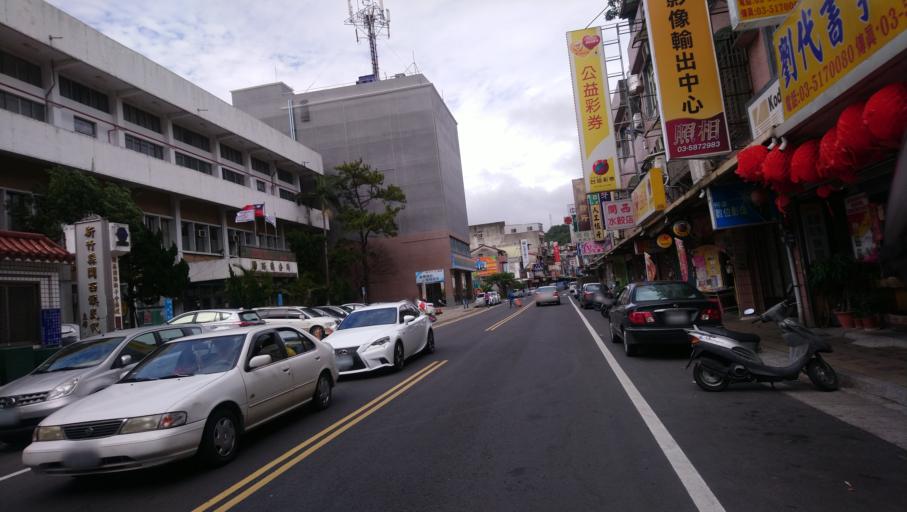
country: TW
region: Taiwan
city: Daxi
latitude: 24.7921
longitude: 121.1761
